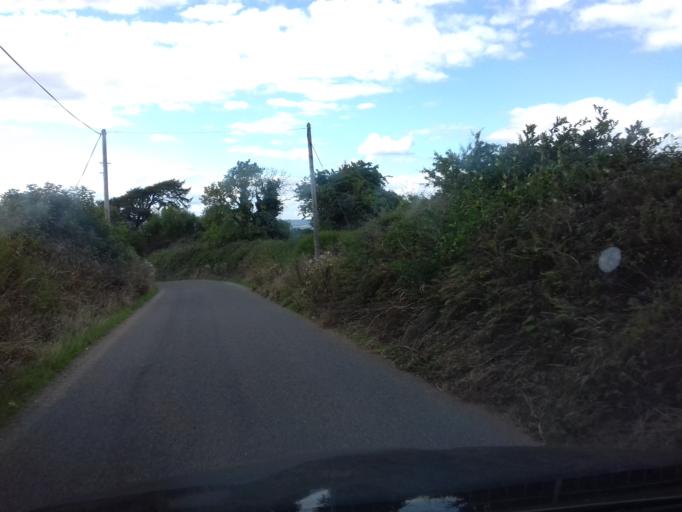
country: IE
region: Leinster
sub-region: Kilkenny
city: Graiguenamanagh
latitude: 52.5774
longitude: -7.0097
